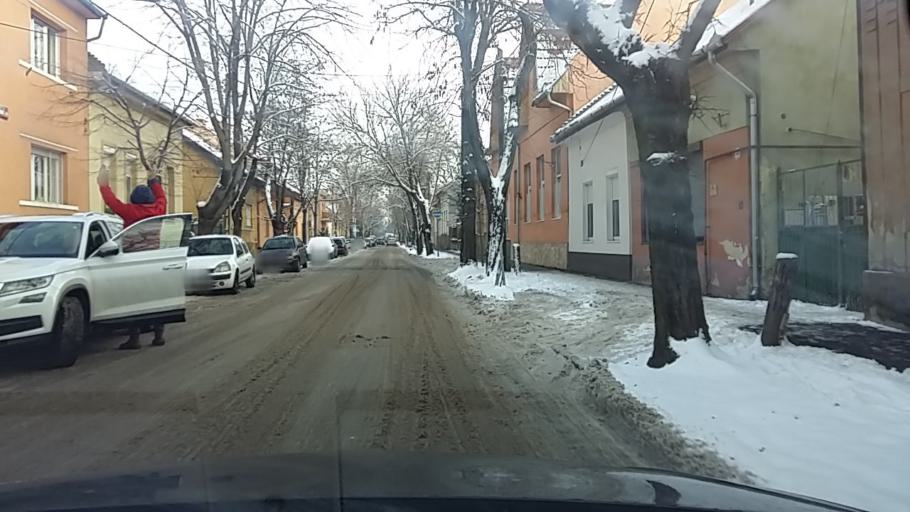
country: HU
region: Budapest
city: Budapest XIX. keruelet
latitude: 47.4522
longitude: 19.1390
